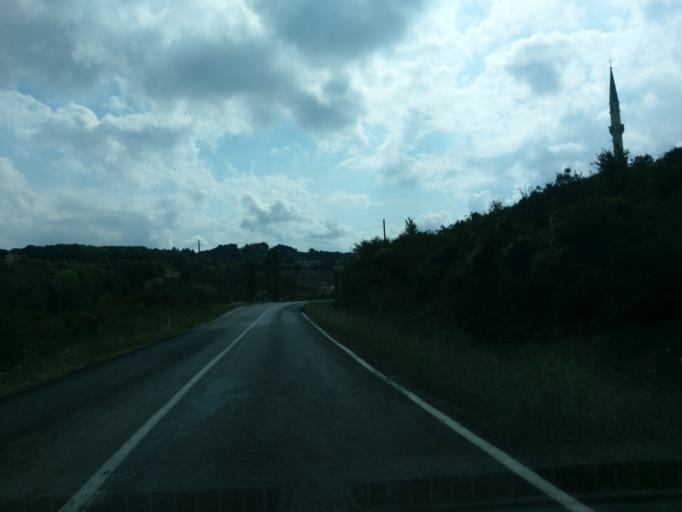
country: TR
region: Sinop
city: Erfelek
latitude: 41.9495
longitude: 34.7709
